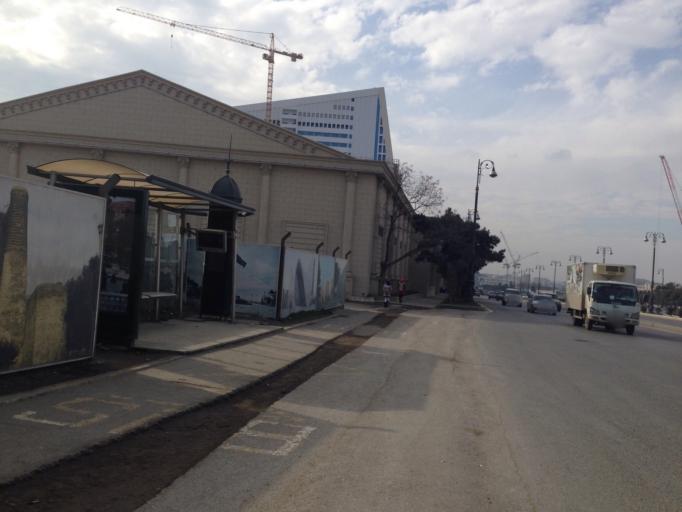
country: AZ
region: Baki
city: Baku
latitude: 40.4138
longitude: 49.9013
